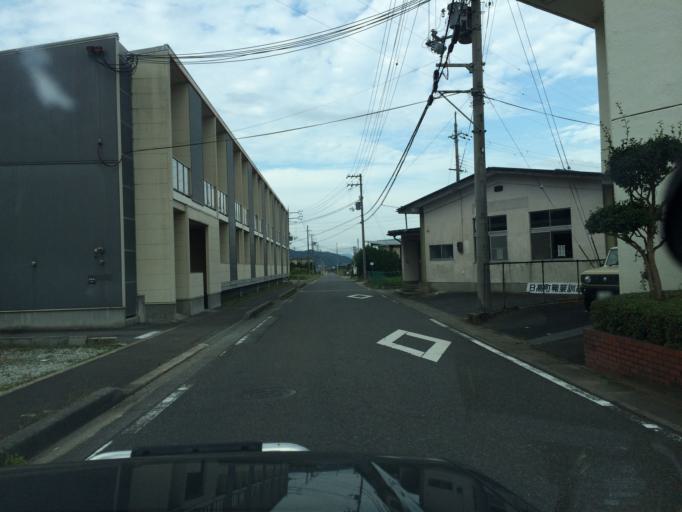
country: JP
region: Hyogo
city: Toyooka
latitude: 35.4727
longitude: 134.7789
